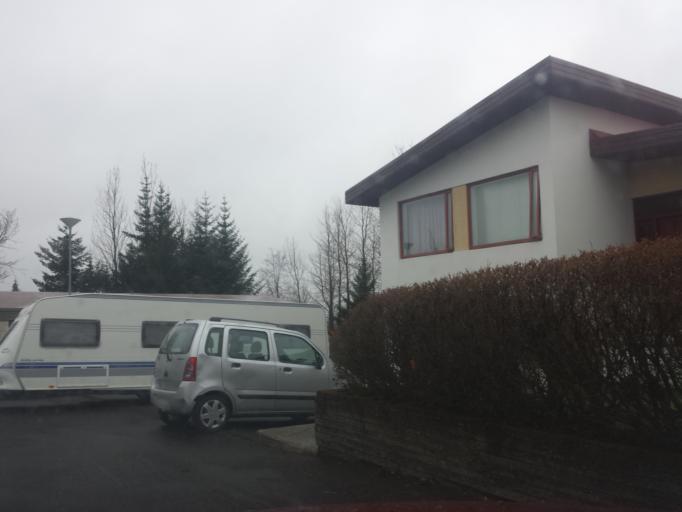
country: IS
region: Capital Region
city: Reykjavik
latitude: 64.1124
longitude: -21.8550
